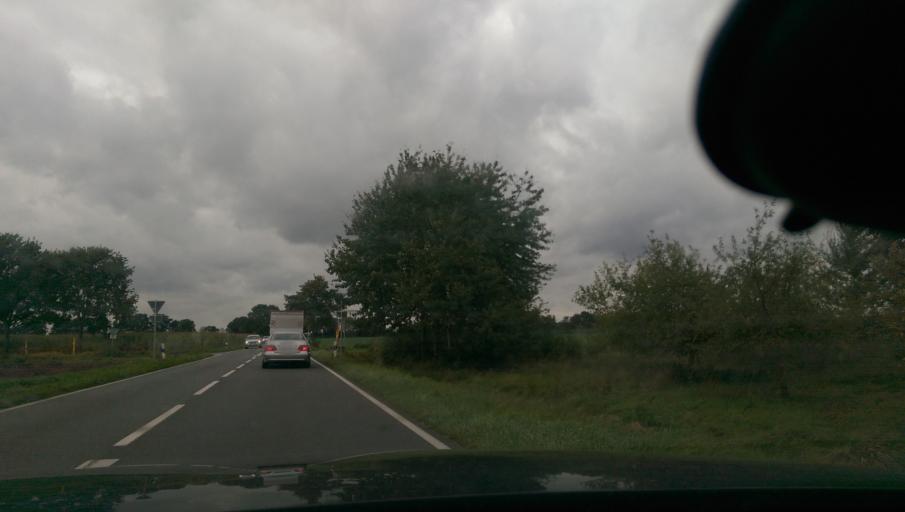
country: DE
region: Lower Saxony
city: Isernhagen Farster Bauerschaft
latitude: 52.4830
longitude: 9.8859
